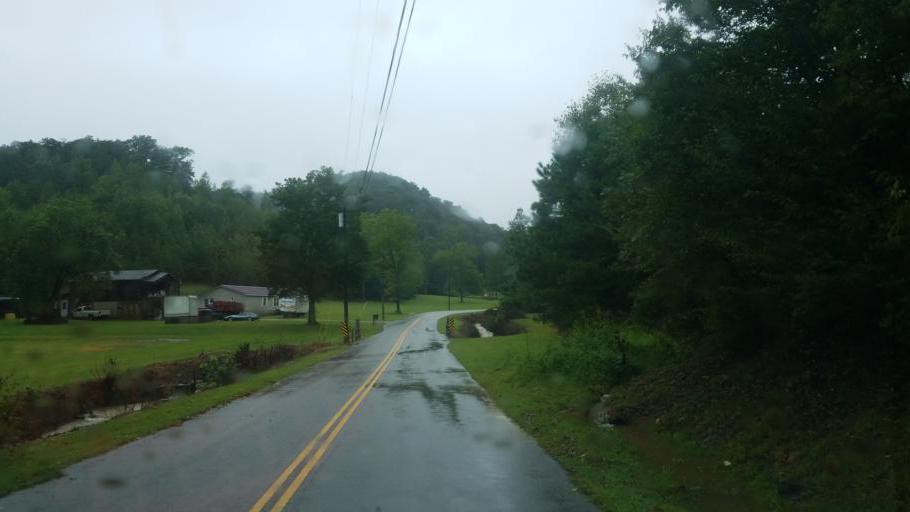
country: US
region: Ohio
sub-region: Scioto County
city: West Portsmouth
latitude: 38.7491
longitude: -83.0960
